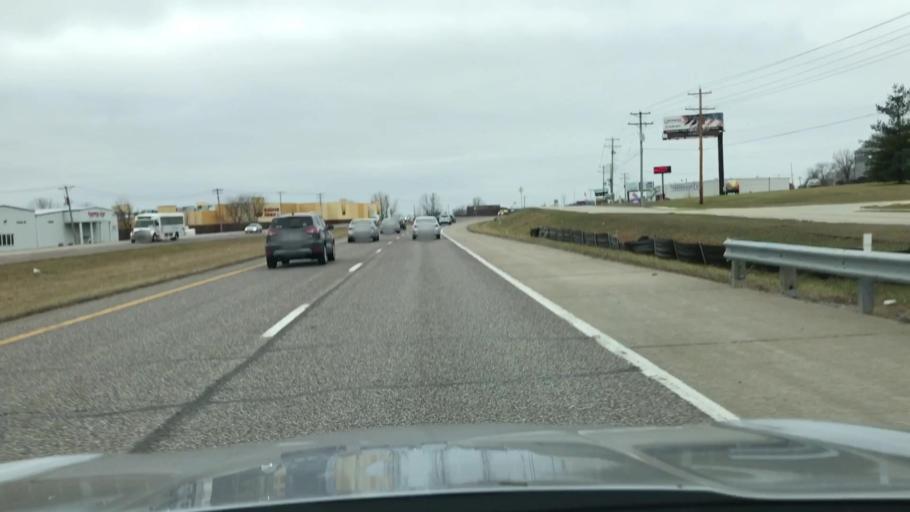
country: US
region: Missouri
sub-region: Saint Charles County
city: Saint Charles
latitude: 38.7652
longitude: -90.5262
